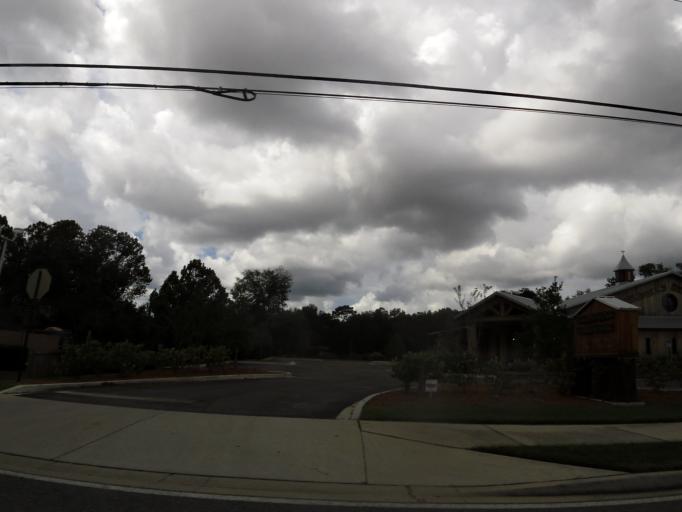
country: US
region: Florida
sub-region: Clay County
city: Asbury Lake
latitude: 30.0500
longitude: -81.8094
